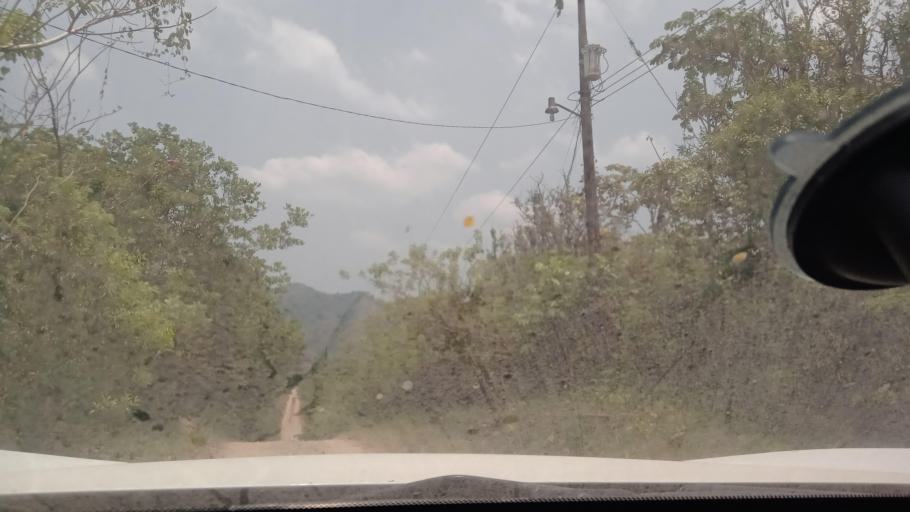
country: MX
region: Chiapas
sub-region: Tecpatan
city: Raudales Malpaso
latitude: 17.4403
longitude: -93.7932
